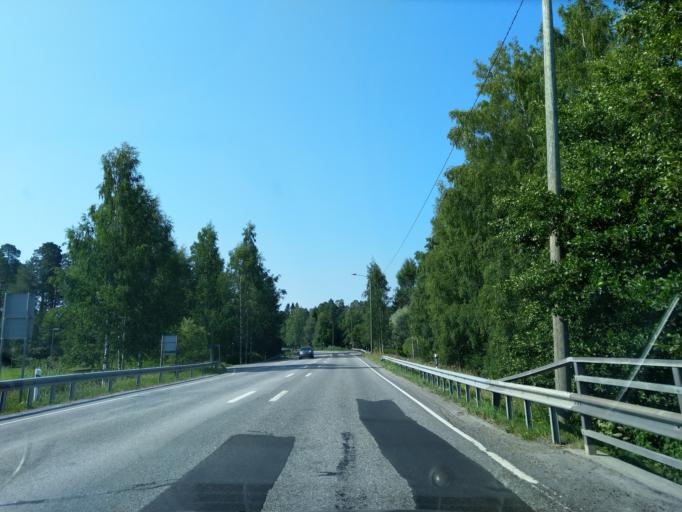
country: FI
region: Satakunta
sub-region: Pori
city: Noormarkku
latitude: 61.5940
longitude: 21.8605
